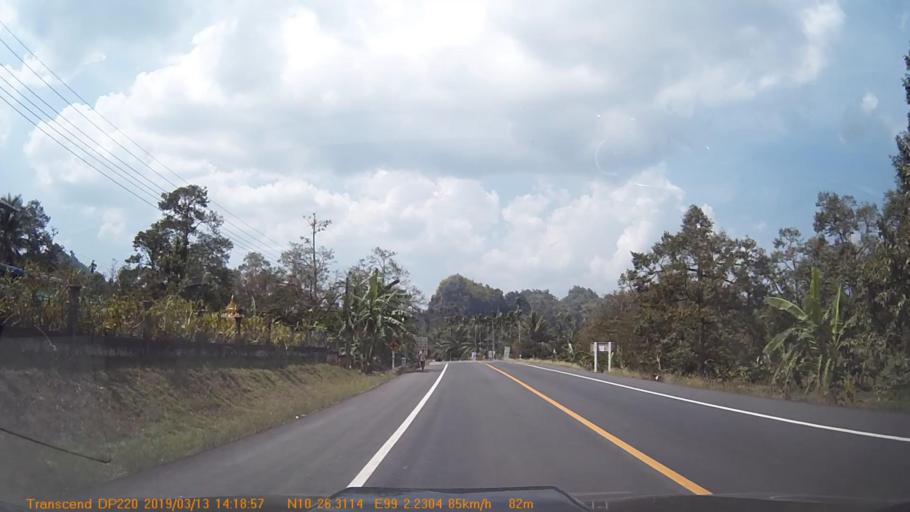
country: TH
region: Chumphon
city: Chumphon
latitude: 10.4390
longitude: 99.0371
